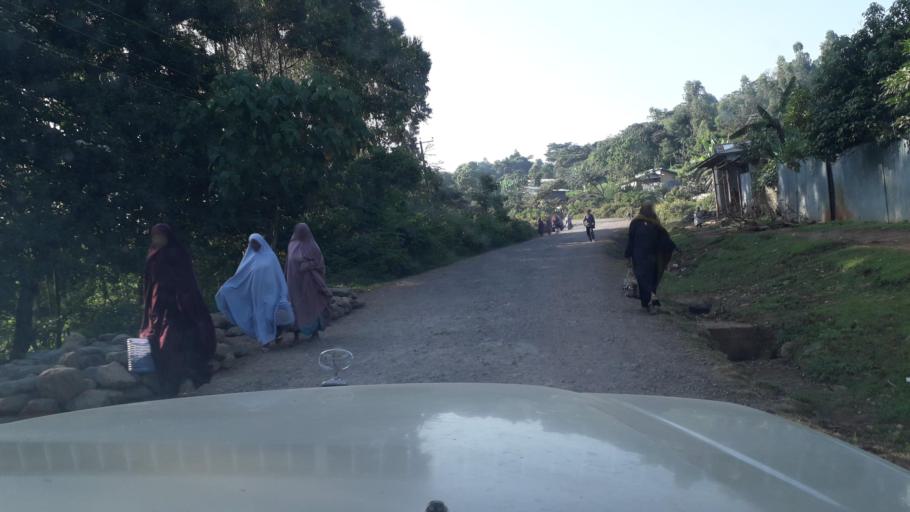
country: ET
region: Oromiya
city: Jima
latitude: 7.4803
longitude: 36.8794
